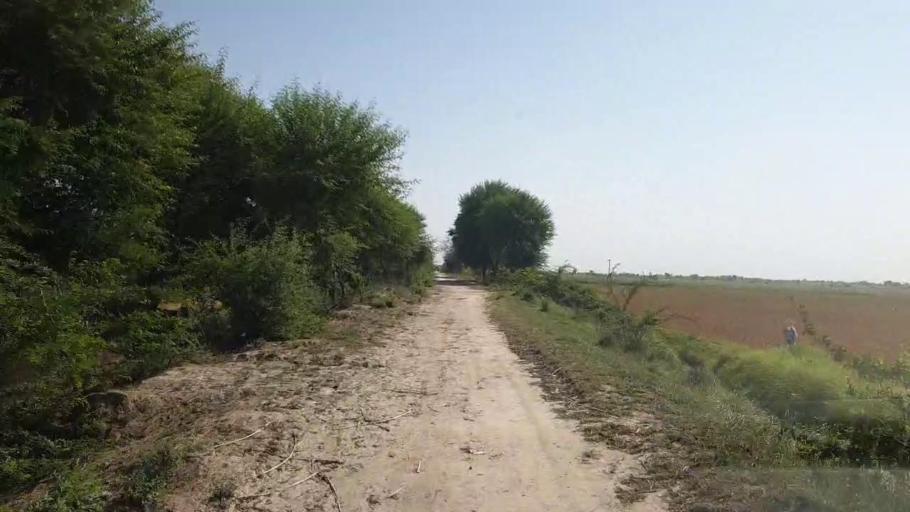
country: PK
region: Sindh
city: Kadhan
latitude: 24.6095
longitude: 69.0001
